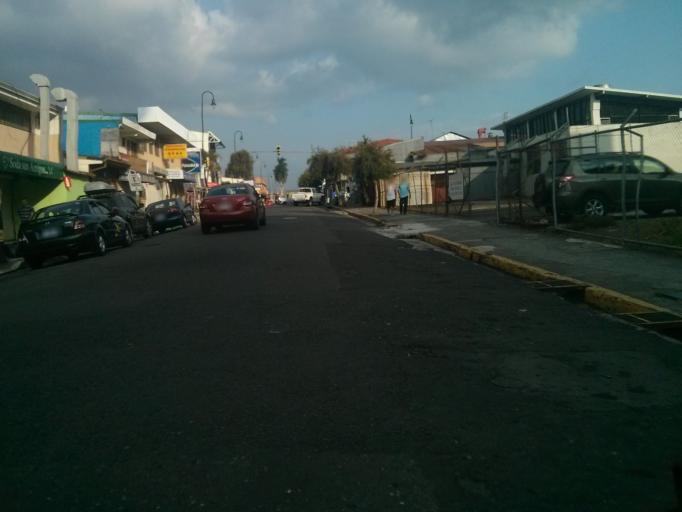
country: CR
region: San Jose
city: Calle Blancos
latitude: 9.9375
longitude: -84.0691
